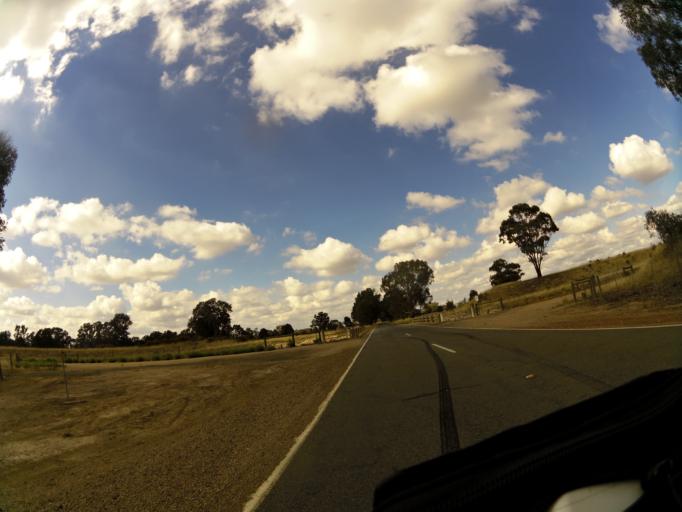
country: AU
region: Victoria
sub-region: Benalla
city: Benalla
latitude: -36.5973
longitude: 146.0107
